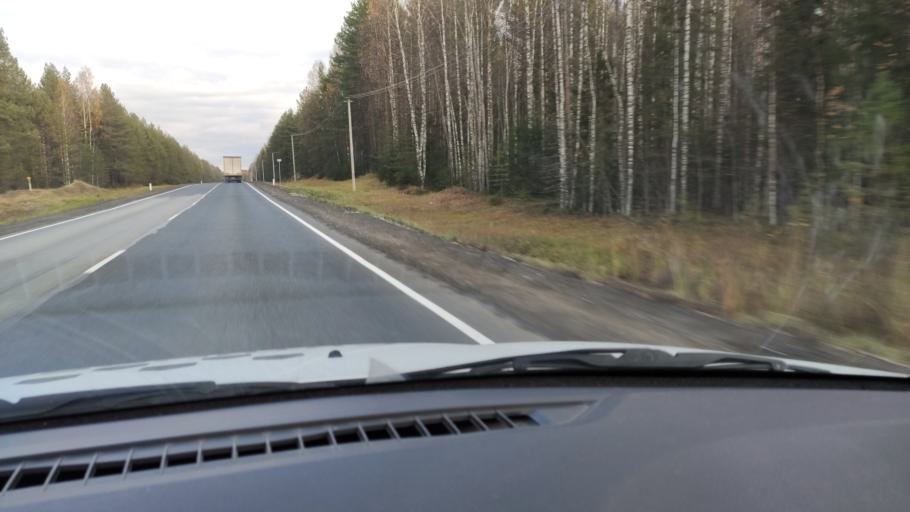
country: RU
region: Kirov
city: Belaya Kholunitsa
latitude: 58.9152
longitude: 51.1527
